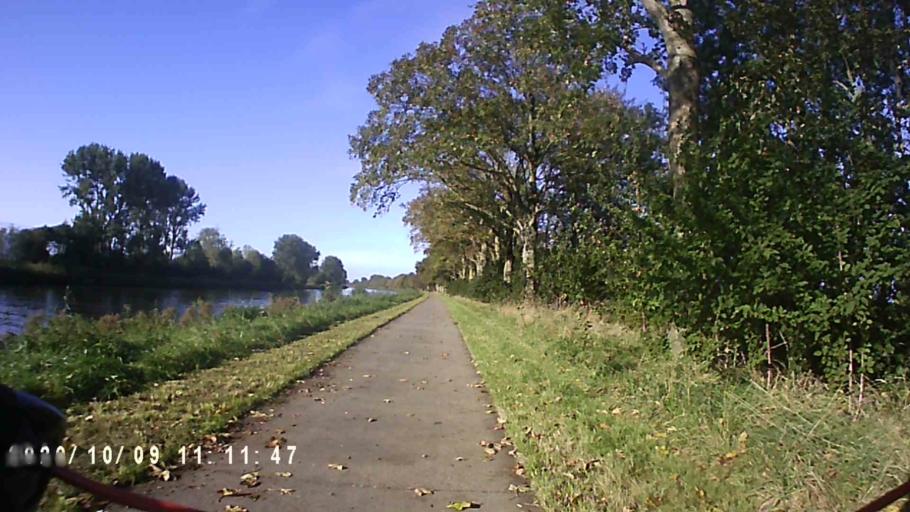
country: NL
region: Groningen
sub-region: Gemeente Zuidhorn
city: Aduard
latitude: 53.2615
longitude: 6.4514
